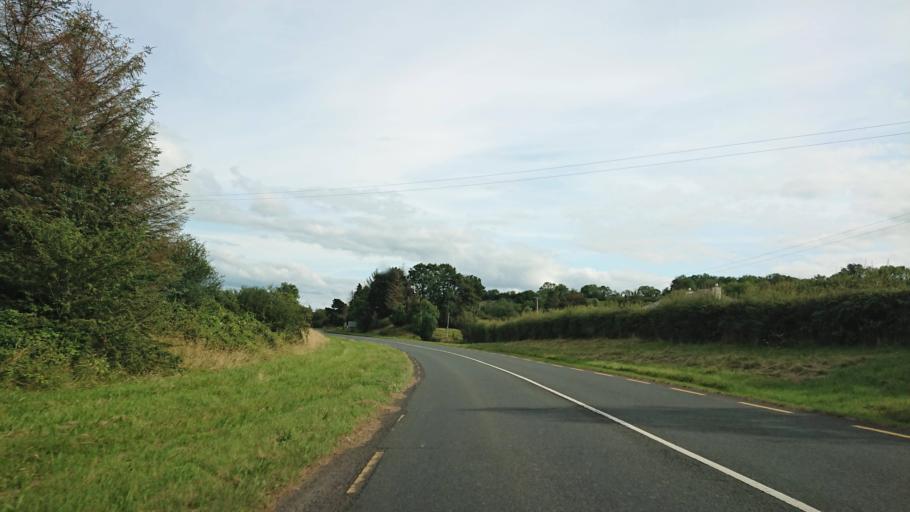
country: IE
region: Connaught
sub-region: County Leitrim
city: Carrick-on-Shannon
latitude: 53.9806
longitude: -8.0650
